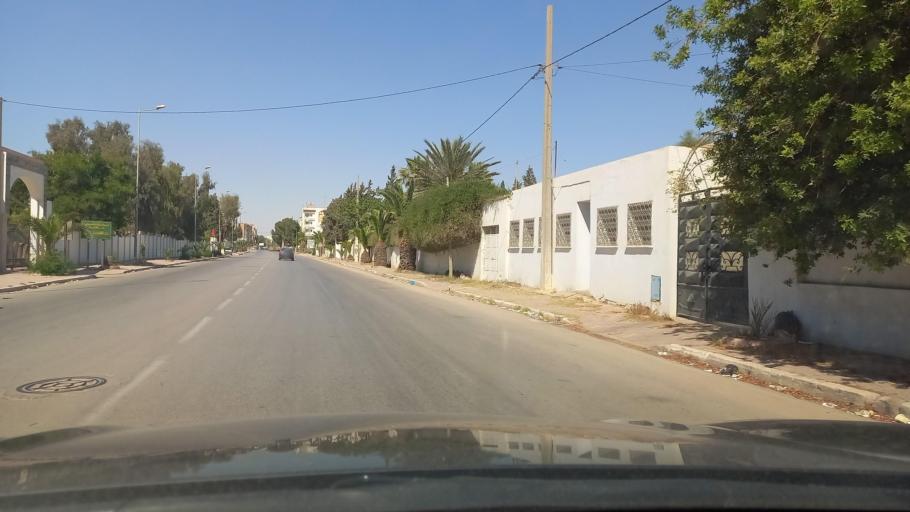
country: TN
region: Safaqis
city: Sfax
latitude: 34.7283
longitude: 10.7290
